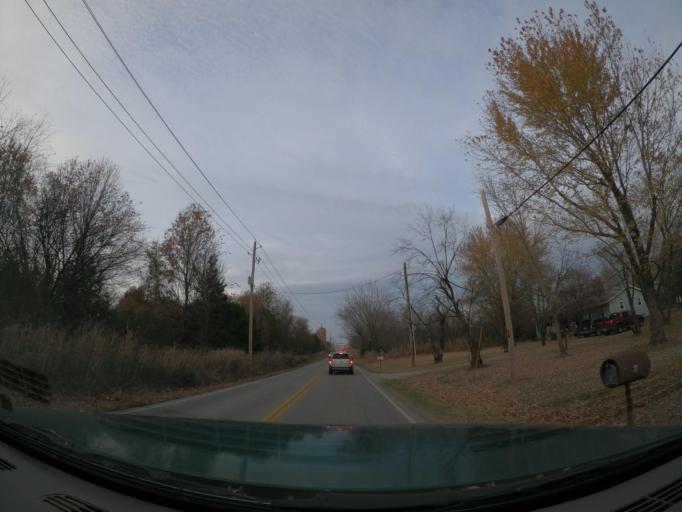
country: US
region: Oklahoma
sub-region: Tulsa County
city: Broken Arrow
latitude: 35.9857
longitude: -95.8153
